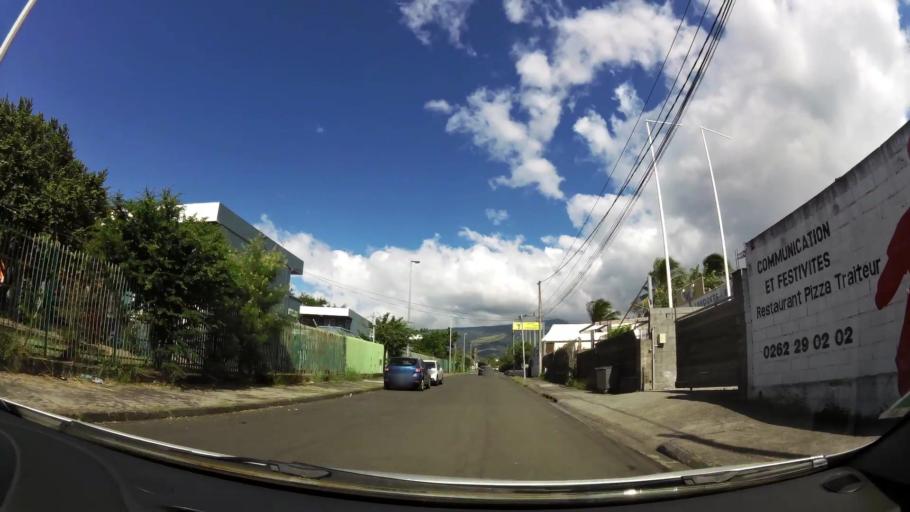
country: RE
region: Reunion
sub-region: Reunion
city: Saint-Denis
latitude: -20.8868
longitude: 55.4956
